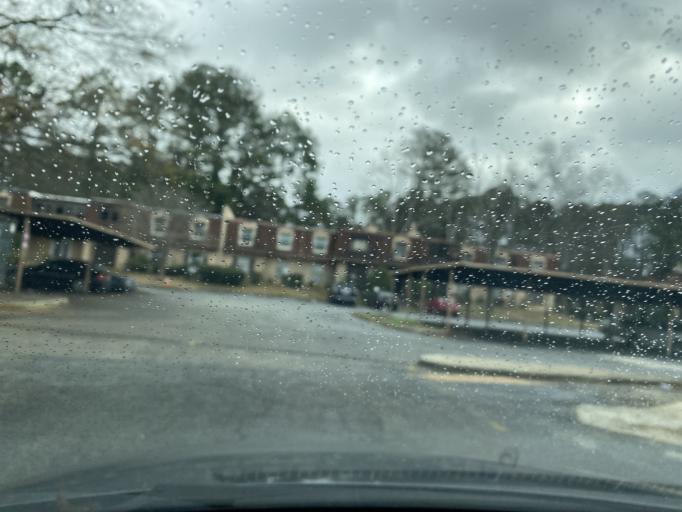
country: US
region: Georgia
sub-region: DeKalb County
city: Pine Mountain
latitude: 33.7004
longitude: -84.1485
